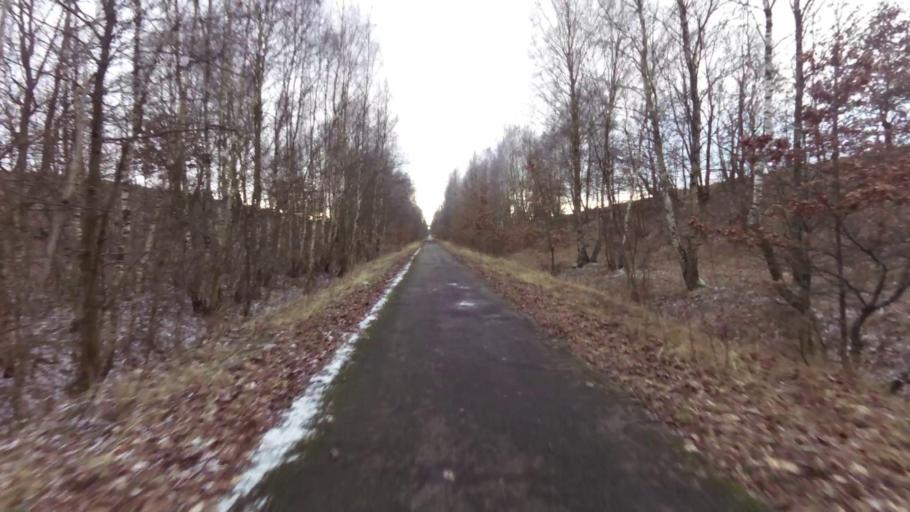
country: PL
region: West Pomeranian Voivodeship
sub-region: Powiat drawski
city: Zlocieniec
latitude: 53.6116
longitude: 16.0508
